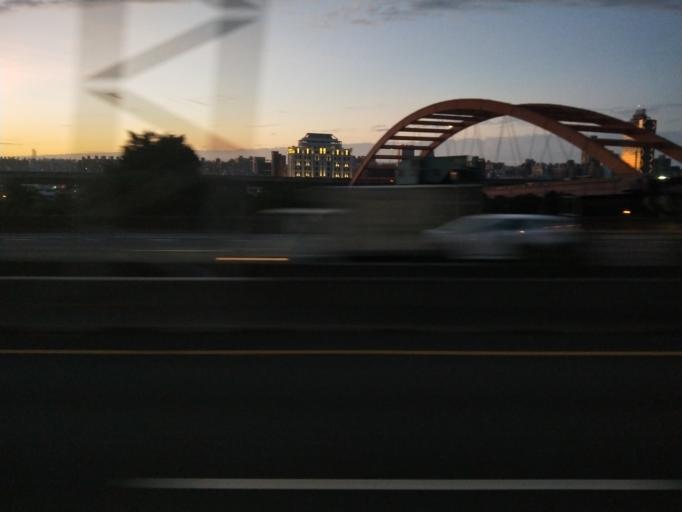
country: TW
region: Taiwan
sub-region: Taichung City
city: Taichung
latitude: 24.1712
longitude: 120.6274
